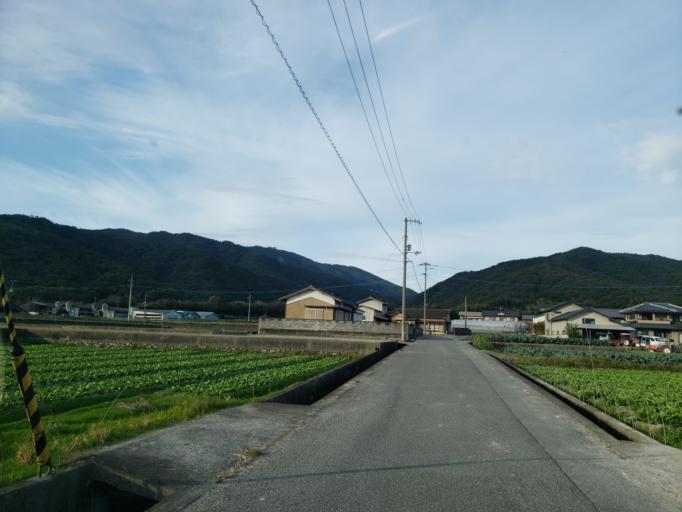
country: JP
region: Tokushima
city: Wakimachi
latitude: 34.0946
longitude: 134.2255
